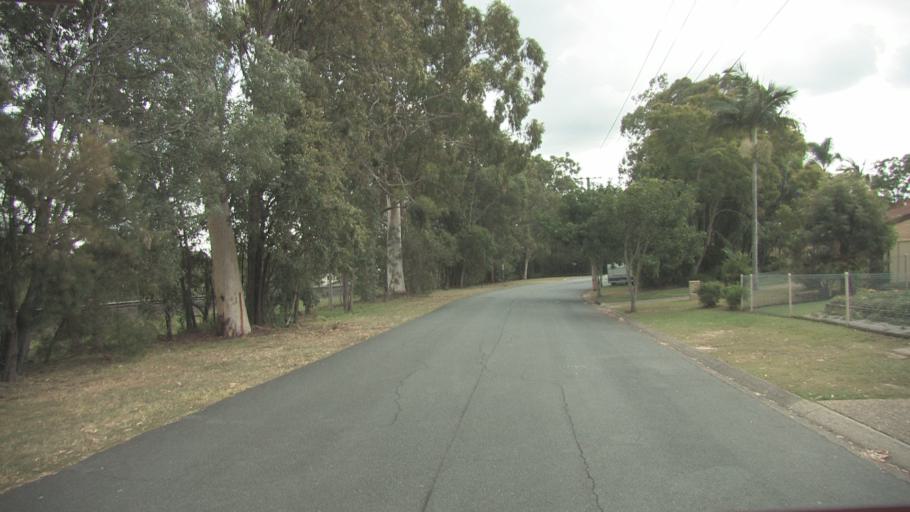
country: AU
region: Queensland
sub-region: Brisbane
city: Forest Lake
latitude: -27.6642
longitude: 153.0192
